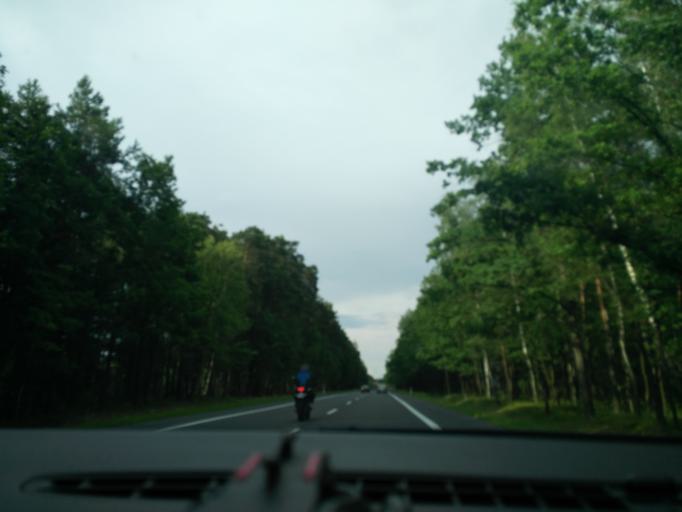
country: PL
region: Subcarpathian Voivodeship
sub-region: Powiat nizanski
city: Zarzecze
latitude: 50.5642
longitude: 22.2480
